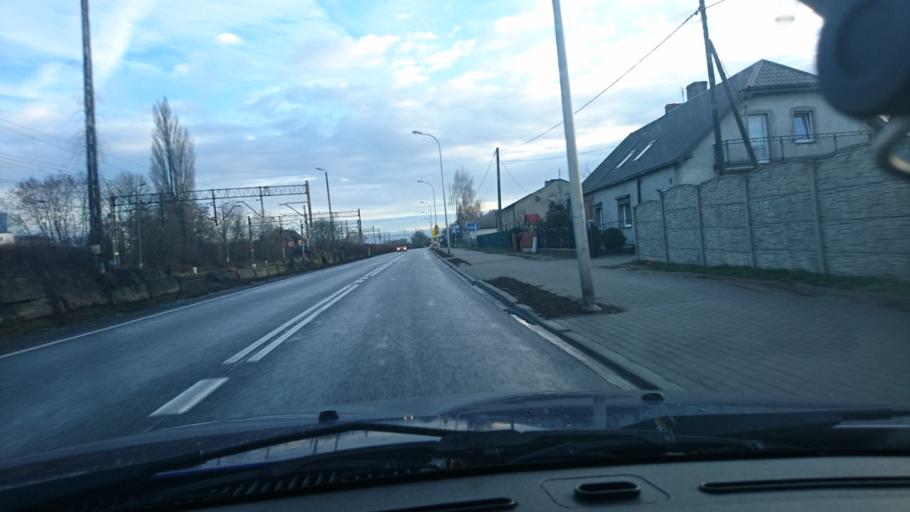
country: PL
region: Greater Poland Voivodeship
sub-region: Powiat kepinski
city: Kepno
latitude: 51.3006
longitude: 17.9955
